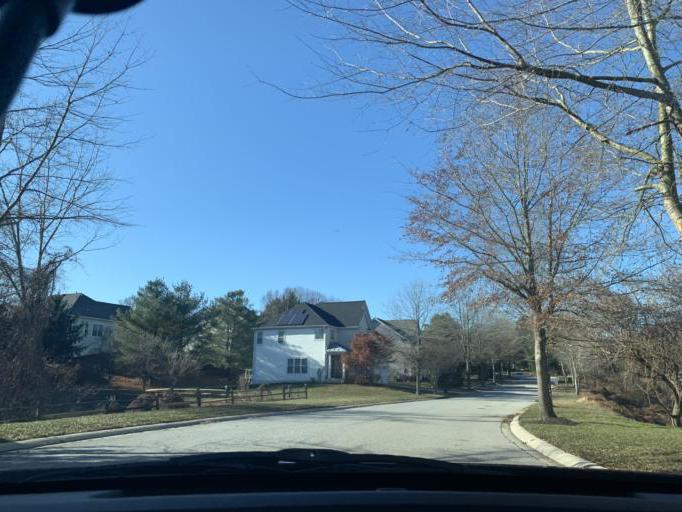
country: US
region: Maryland
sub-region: Baltimore County
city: Garrison
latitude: 39.3977
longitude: -76.7353
